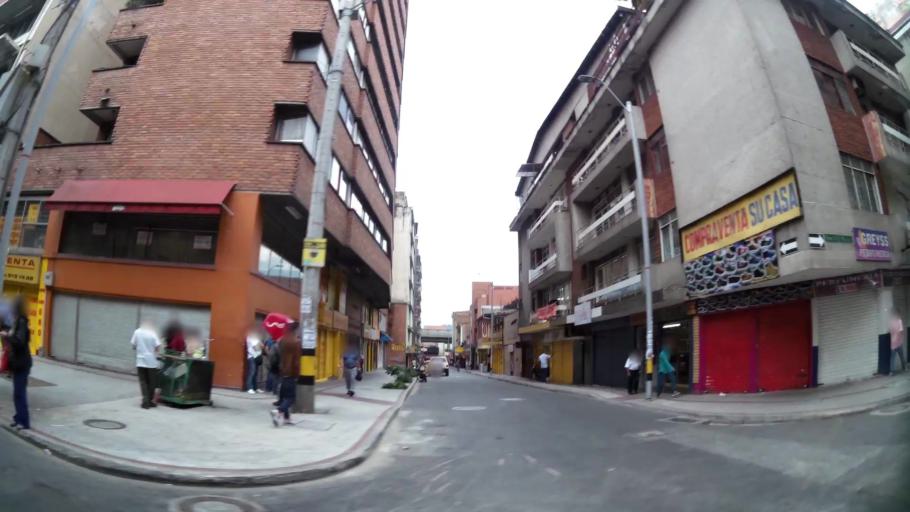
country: CO
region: Antioquia
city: Medellin
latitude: 6.2531
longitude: -75.5664
